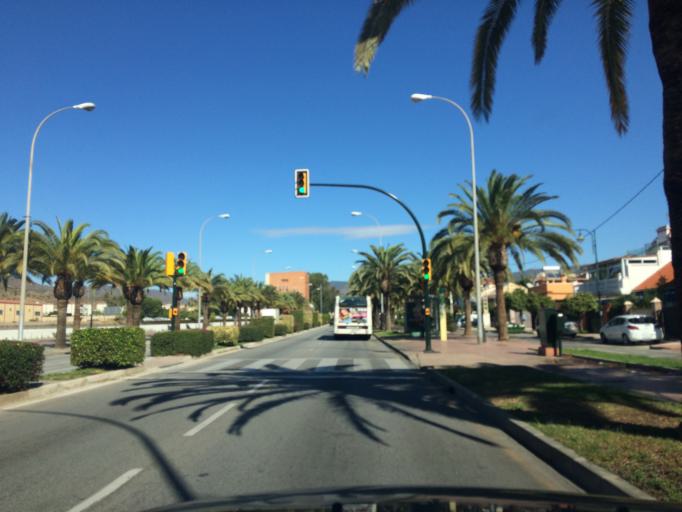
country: ES
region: Andalusia
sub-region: Provincia de Malaga
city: Malaga
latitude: 36.7351
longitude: -4.4248
